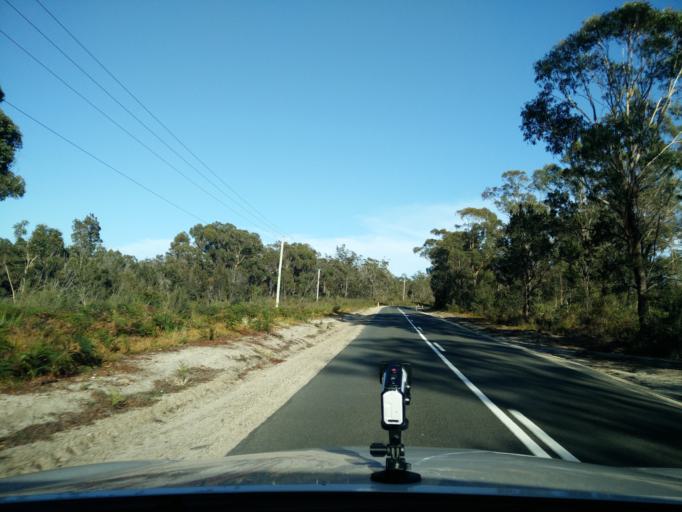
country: AU
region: Tasmania
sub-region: Break O'Day
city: St Helens
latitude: -41.2898
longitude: 148.1746
